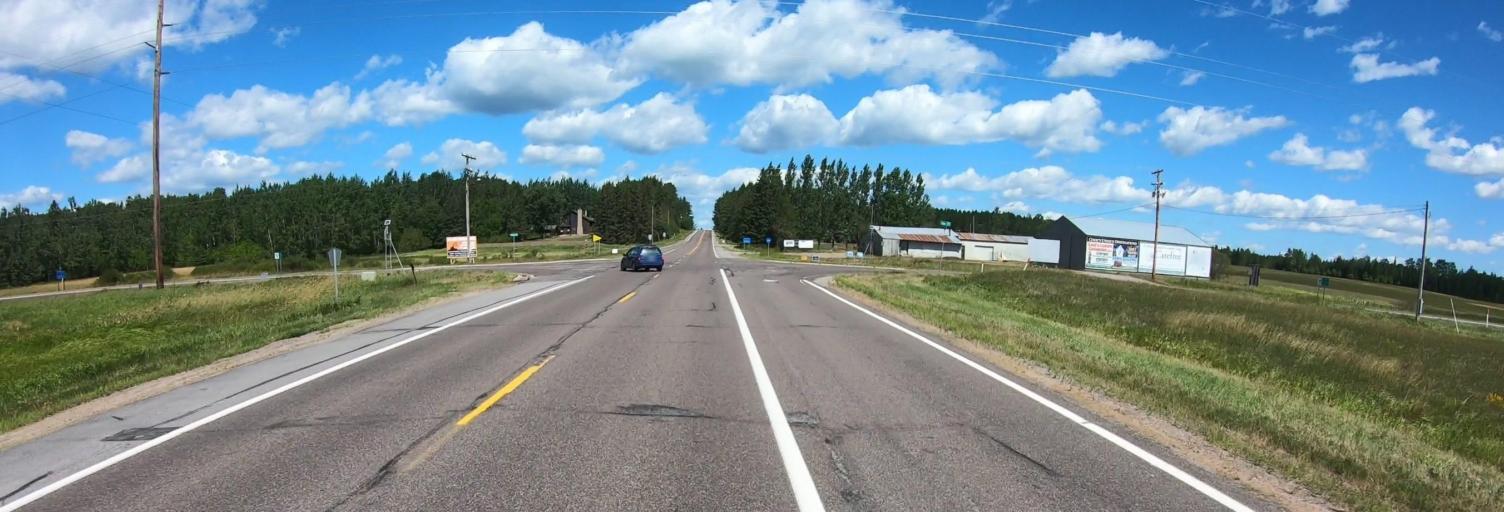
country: US
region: Minnesota
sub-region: Saint Louis County
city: Mountain Iron
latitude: 47.8604
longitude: -92.6855
